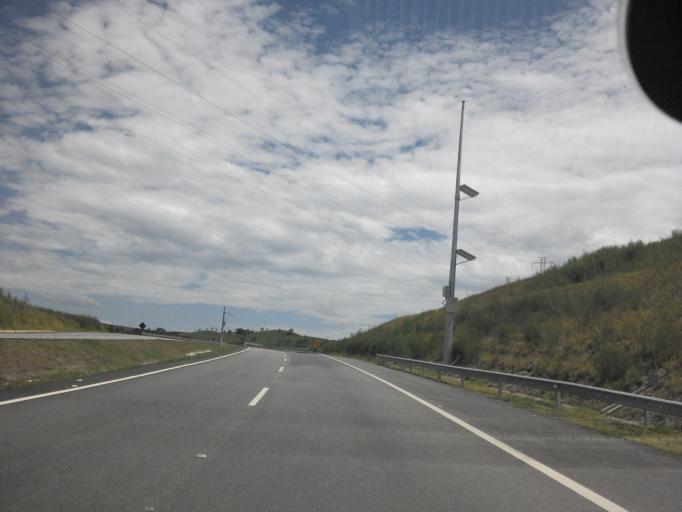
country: BR
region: Sao Paulo
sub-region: Taubate
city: Taubate
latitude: -23.0866
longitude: -45.5570
